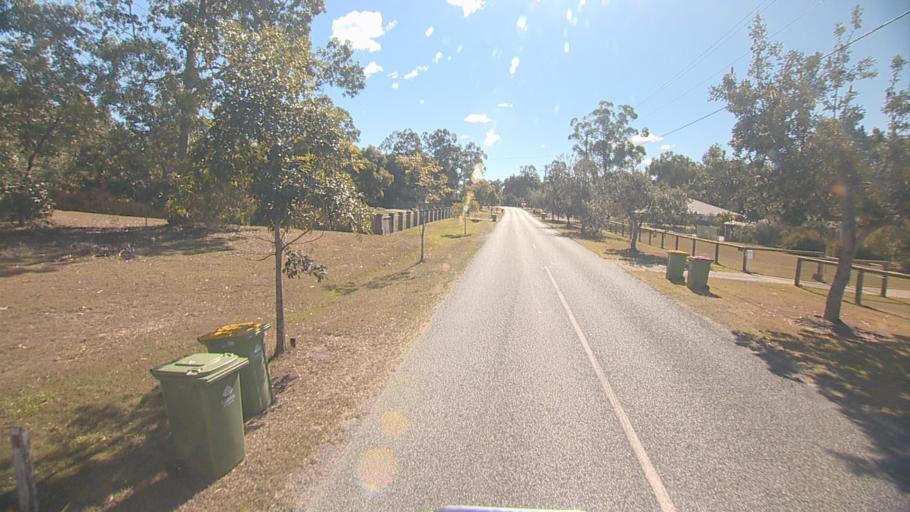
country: AU
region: Queensland
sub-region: Logan
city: North Maclean
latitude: -27.7463
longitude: 152.9557
